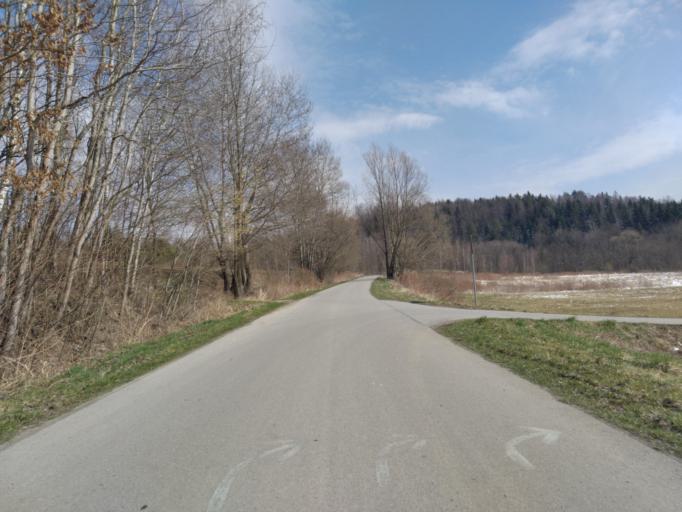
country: PL
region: Subcarpathian Voivodeship
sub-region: Powiat ropczycko-sedziszowski
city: Ropczyce
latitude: 50.0084
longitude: 21.5833
